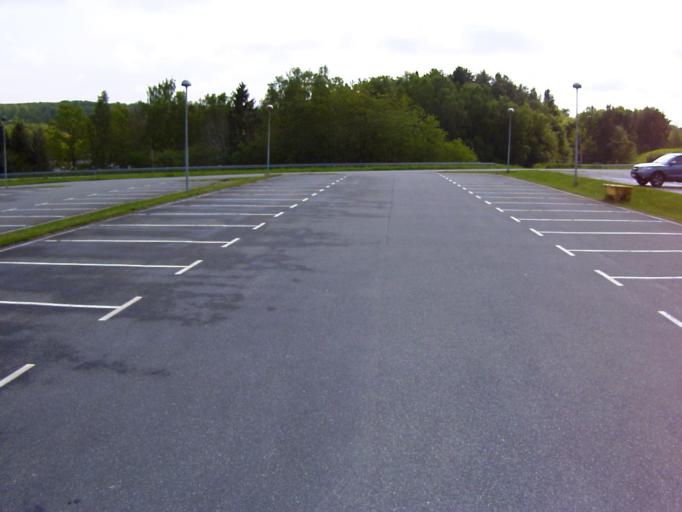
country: SE
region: Skane
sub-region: Kristianstads Kommun
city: Degeberga
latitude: 55.8254
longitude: 14.0771
